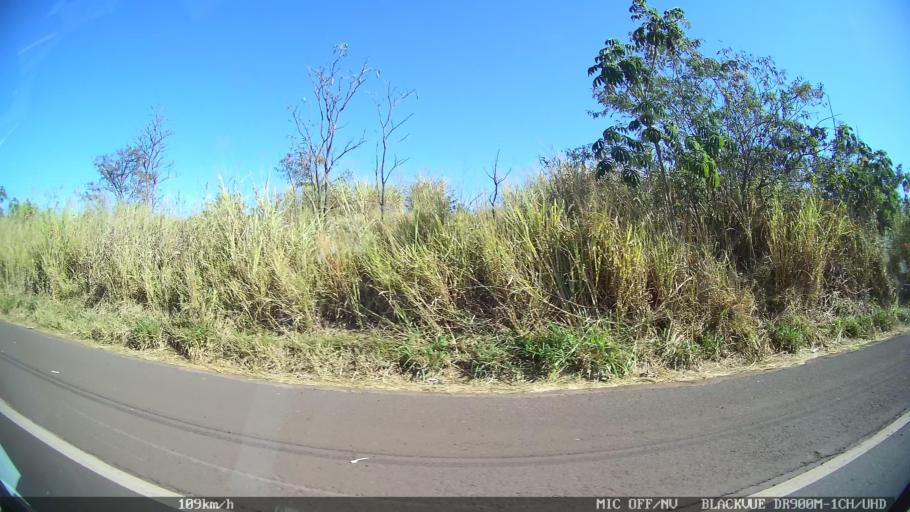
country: BR
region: Sao Paulo
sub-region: Olimpia
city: Olimpia
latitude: -20.7159
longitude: -48.8746
